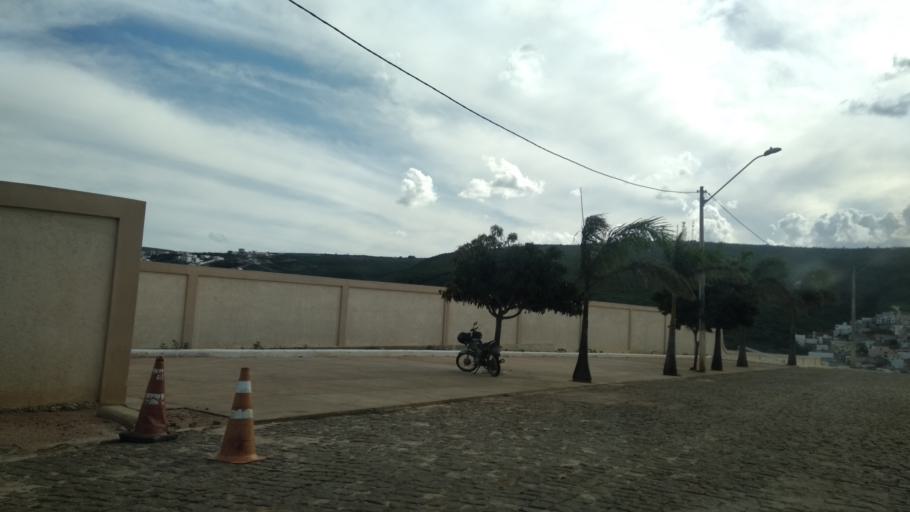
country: BR
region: Bahia
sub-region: Caetite
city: Caetite
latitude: -14.0617
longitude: -42.4929
